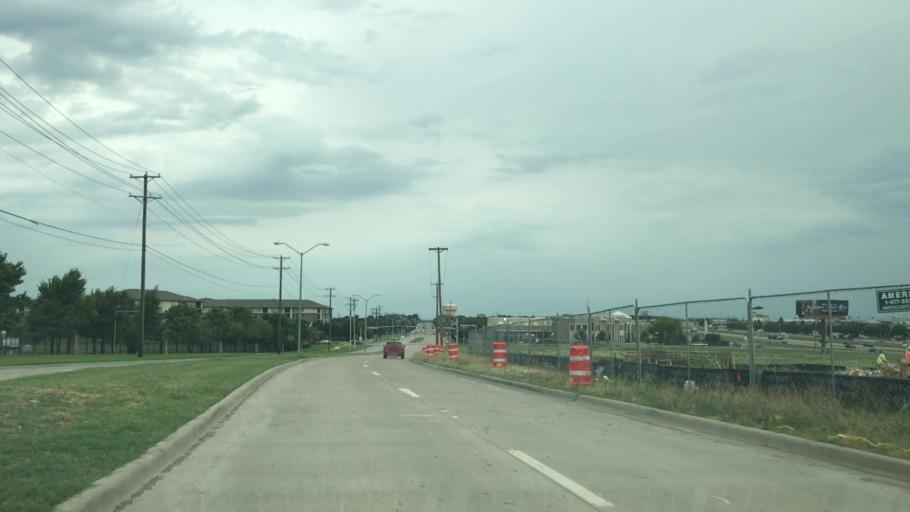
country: US
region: Texas
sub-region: Dallas County
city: Richardson
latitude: 32.9976
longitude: -96.7593
